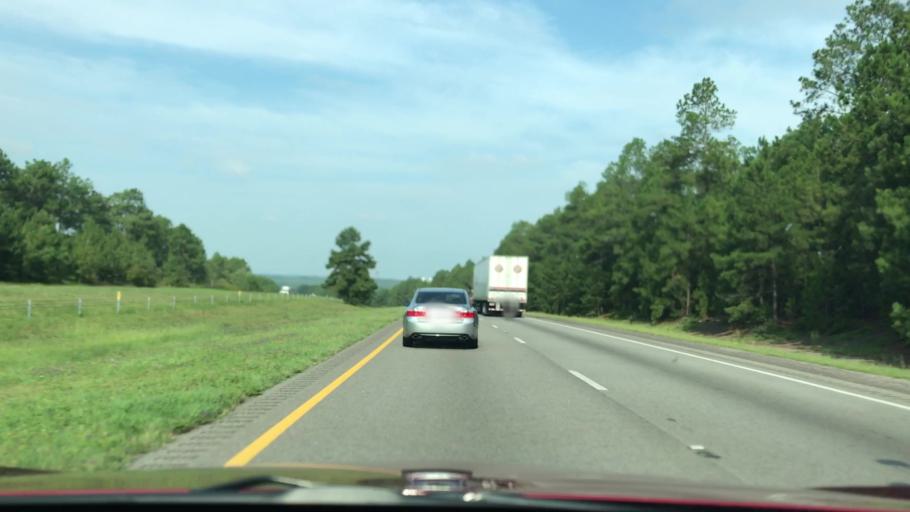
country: US
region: South Carolina
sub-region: Aiken County
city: Graniteville
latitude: 33.6334
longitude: -81.7867
